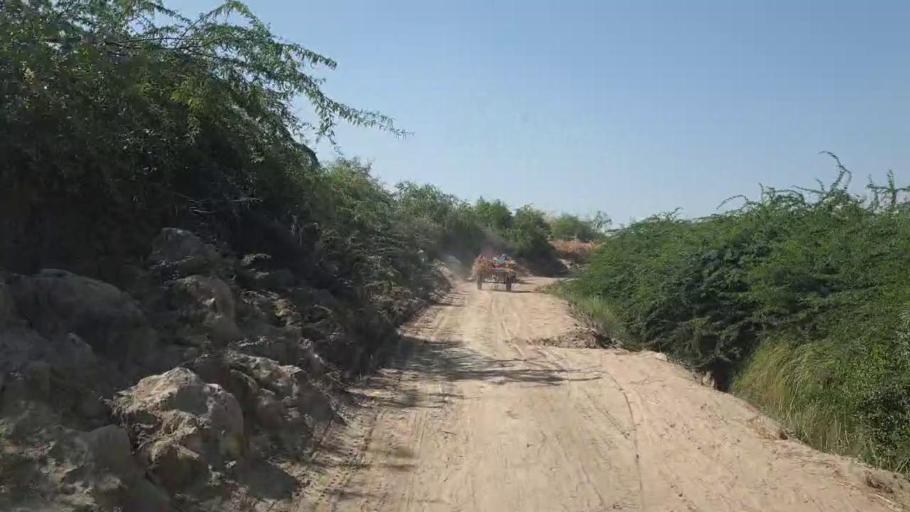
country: PK
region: Sindh
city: Talhar
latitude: 24.8060
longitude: 68.7949
